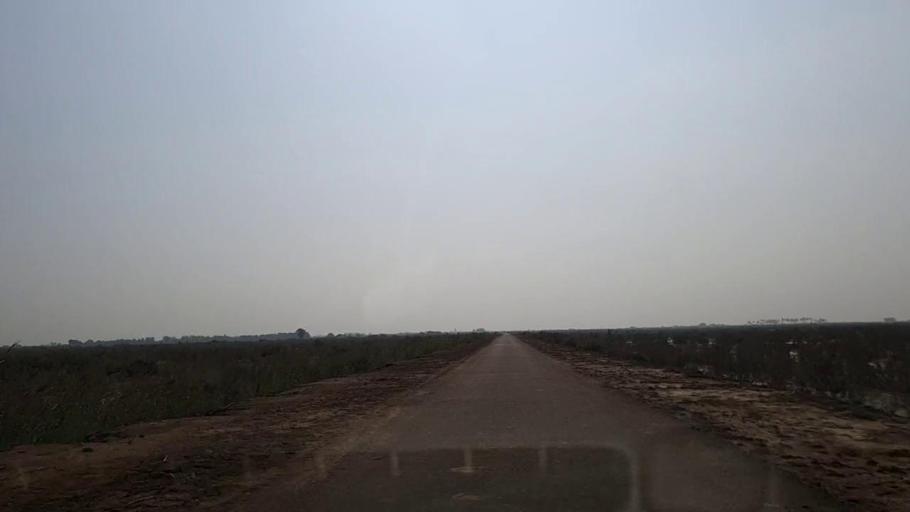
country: PK
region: Sindh
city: Gharo
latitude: 24.6655
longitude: 67.6945
